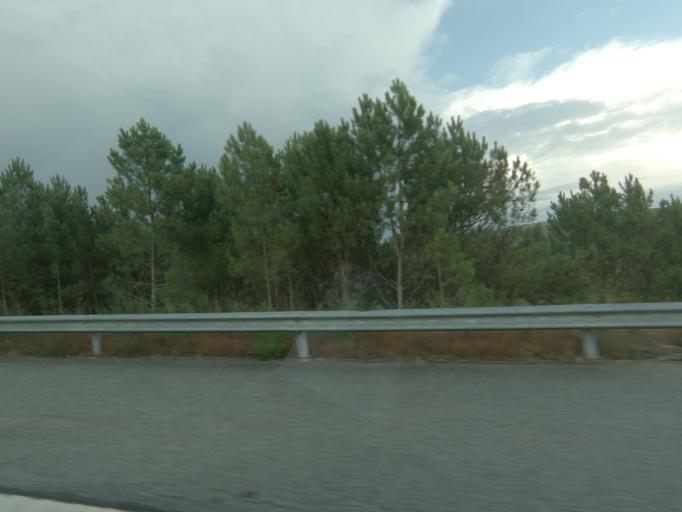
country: PT
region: Viseu
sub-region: Castro Daire
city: Castro Daire
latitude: 40.9131
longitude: -7.9090
